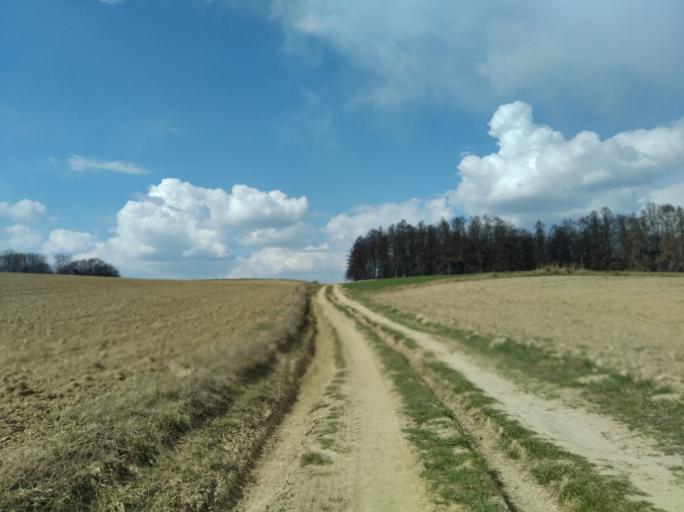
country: PL
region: Subcarpathian Voivodeship
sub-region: Powiat strzyzowski
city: Strzyzow
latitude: 49.9200
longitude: 21.7433
